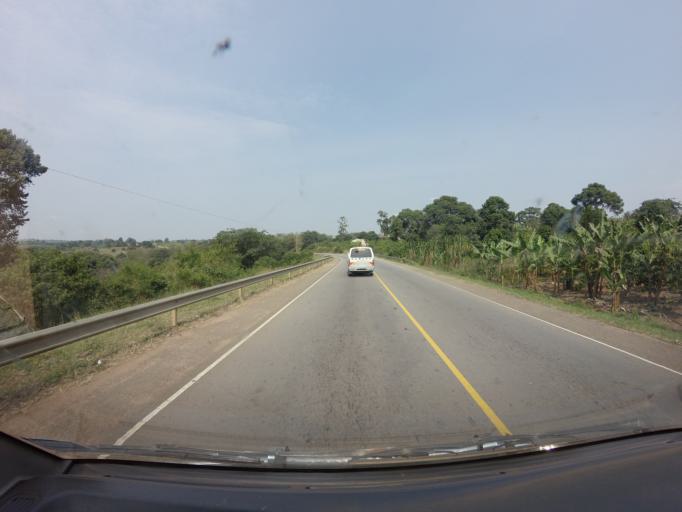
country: UG
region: Central Region
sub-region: Lwengo District
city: Lwengo
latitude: -0.3969
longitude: 31.4217
